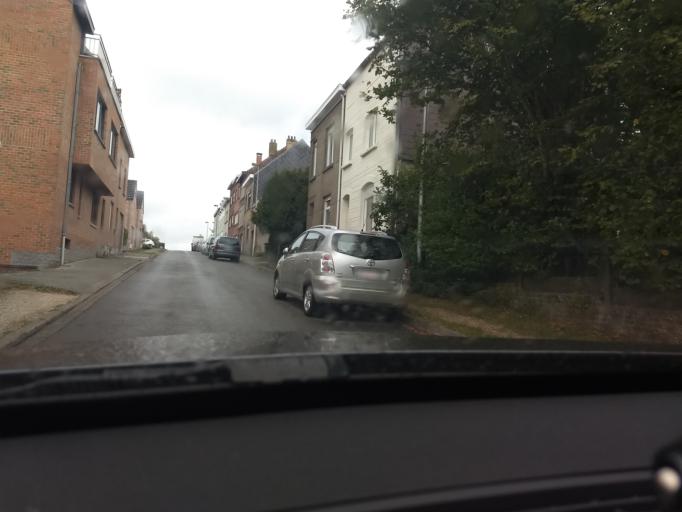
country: BE
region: Wallonia
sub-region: Province du Brabant Wallon
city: Braine-l'Alleud
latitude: 50.6752
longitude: 4.3727
